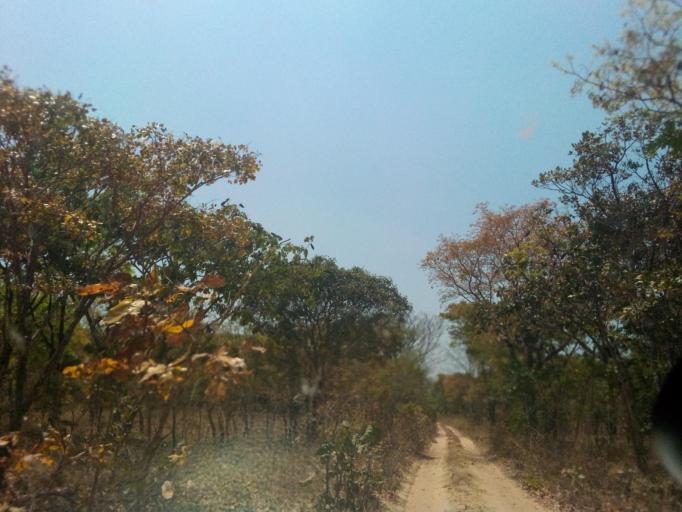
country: ZM
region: Copperbelt
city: Kataba
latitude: -12.2510
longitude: 30.3910
